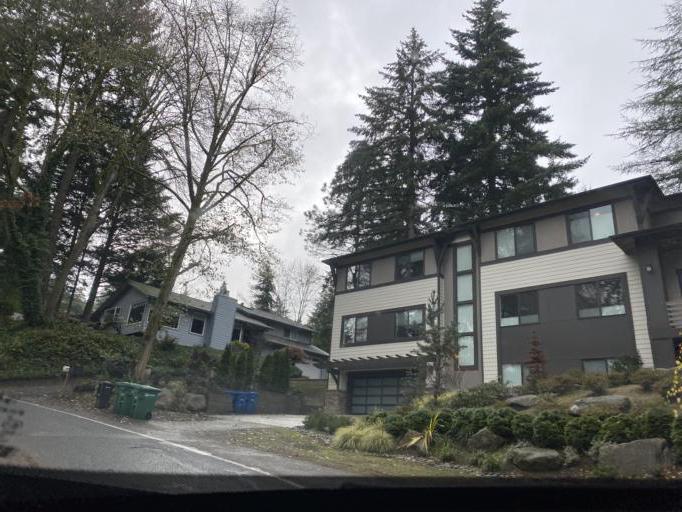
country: US
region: Washington
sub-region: King County
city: Mercer Island
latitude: 47.5404
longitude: -122.2140
